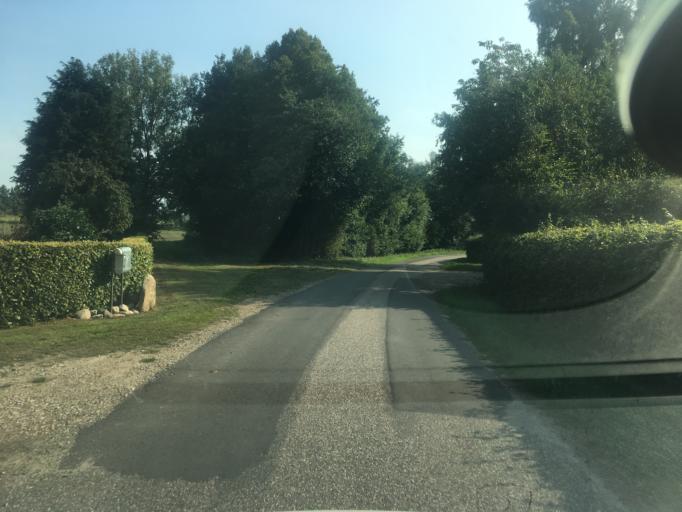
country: DK
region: South Denmark
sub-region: Tonder Kommune
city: Logumkloster
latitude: 54.9977
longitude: 8.9242
